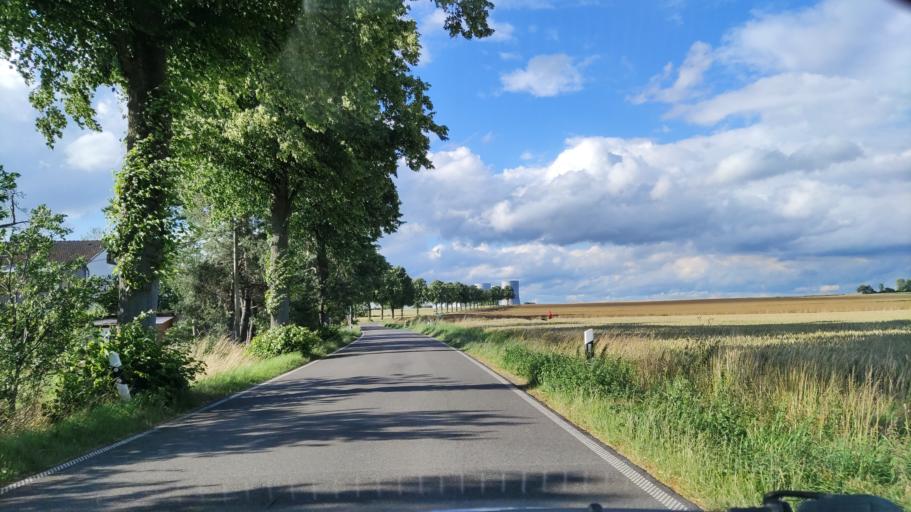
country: DE
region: North Rhine-Westphalia
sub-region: Regierungsbezirk Arnsberg
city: Welver
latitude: 51.6521
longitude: 7.9661
